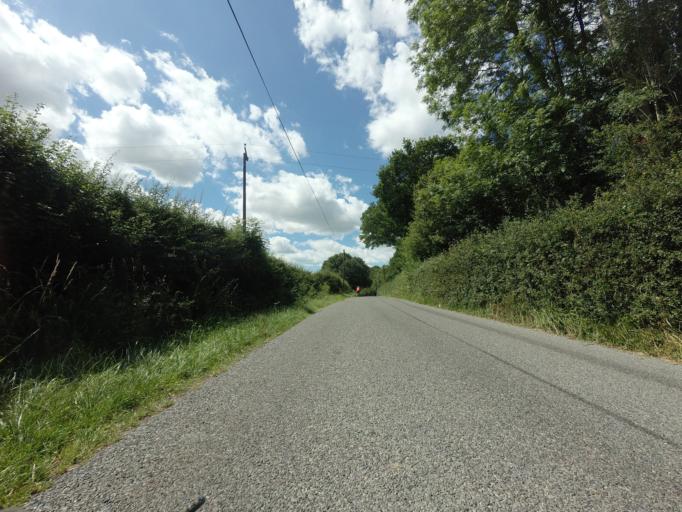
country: GB
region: England
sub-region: East Sussex
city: Hailsham
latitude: 50.8736
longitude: 0.1718
